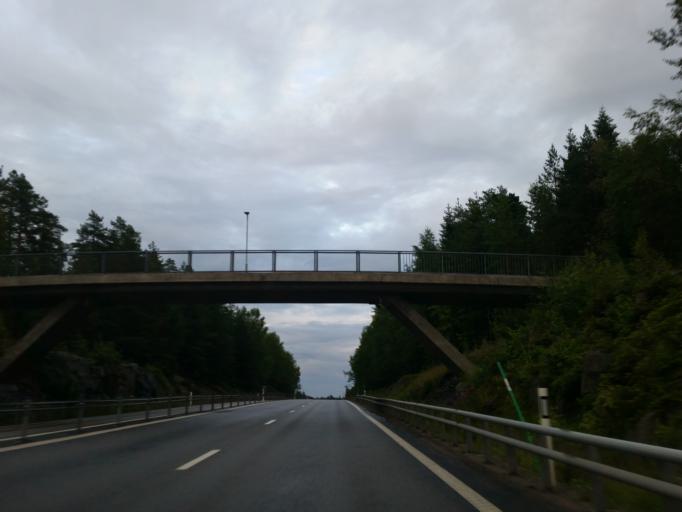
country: SE
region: Vaesterbotten
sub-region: Umea Kommun
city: Ersmark
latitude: 63.8478
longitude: 20.3263
